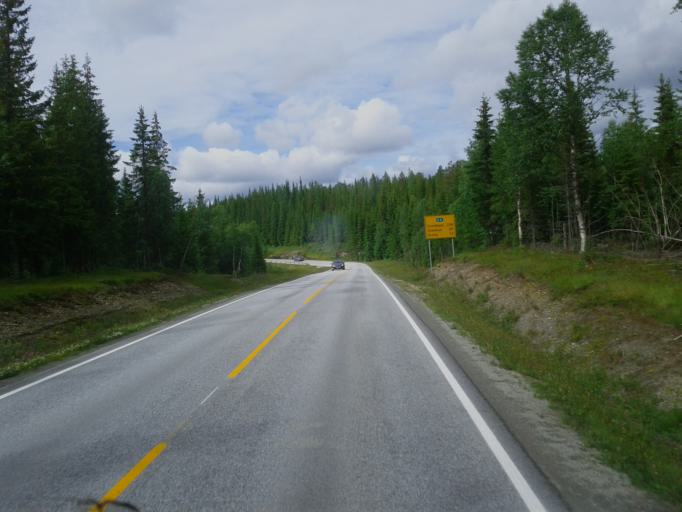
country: NO
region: Nord-Trondelag
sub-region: Hoylandet
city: Hoylandet
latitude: 64.6915
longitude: 12.7486
